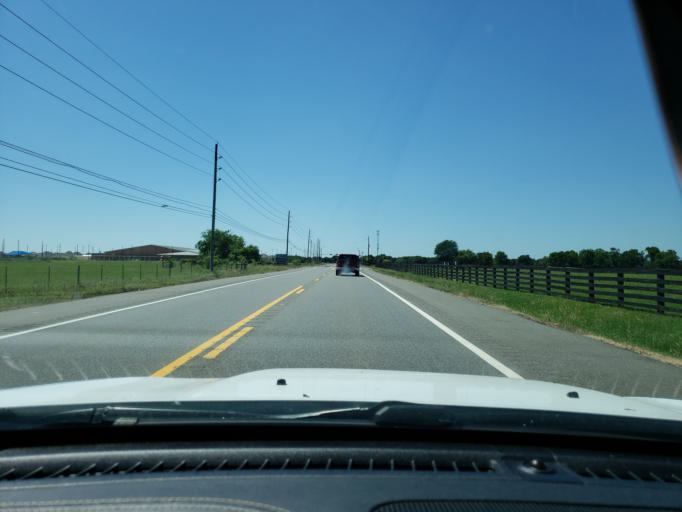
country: US
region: Texas
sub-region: Fort Bend County
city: Fulshear
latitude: 29.6742
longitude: -95.8389
